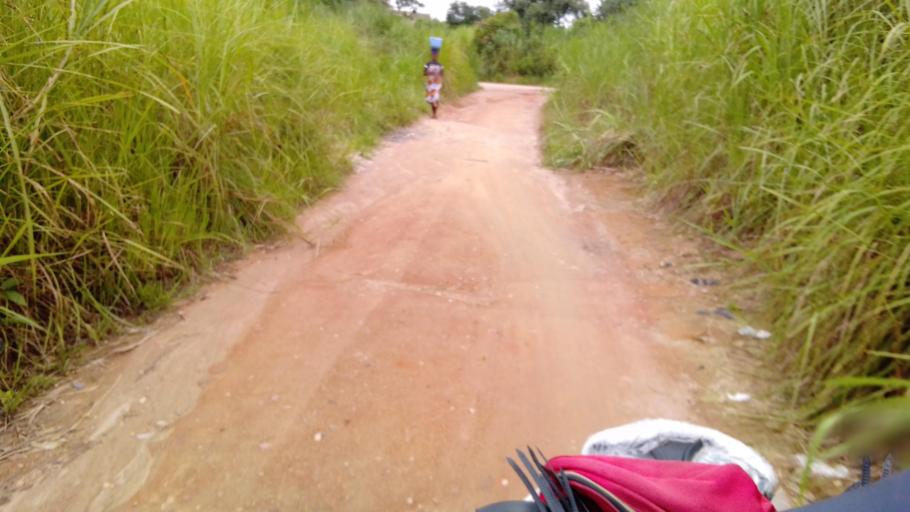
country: SL
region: Eastern Province
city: Koidu
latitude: 8.6745
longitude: -10.9842
